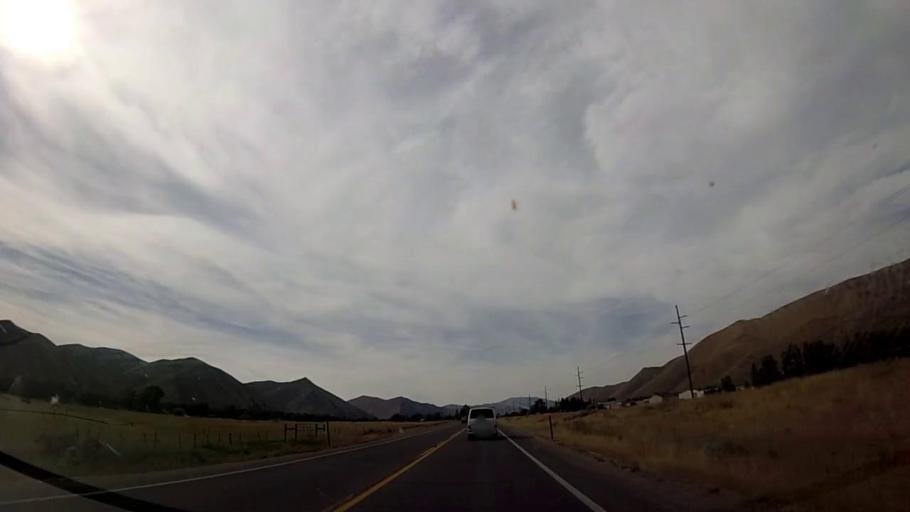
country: US
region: Idaho
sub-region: Blaine County
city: Bellevue
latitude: 43.4826
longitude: -114.2732
